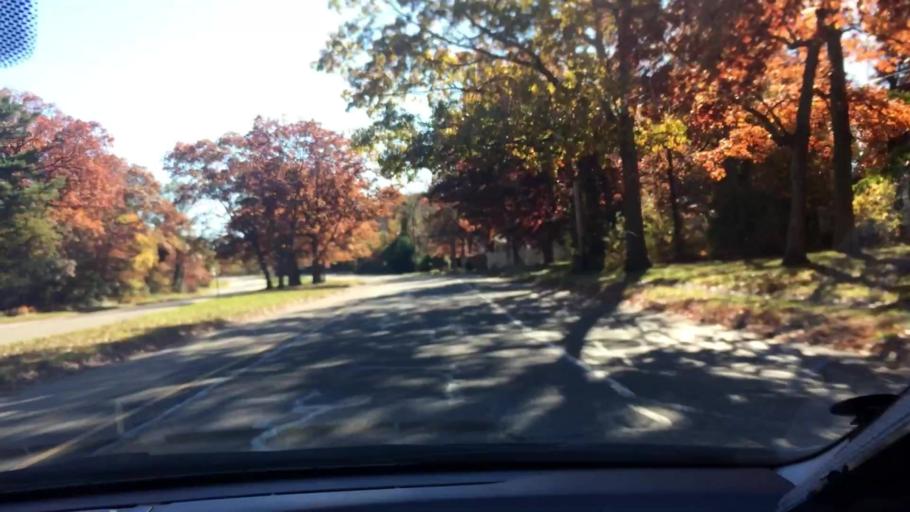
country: US
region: New York
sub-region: Suffolk County
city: West Babylon
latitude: 40.7368
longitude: -73.3465
